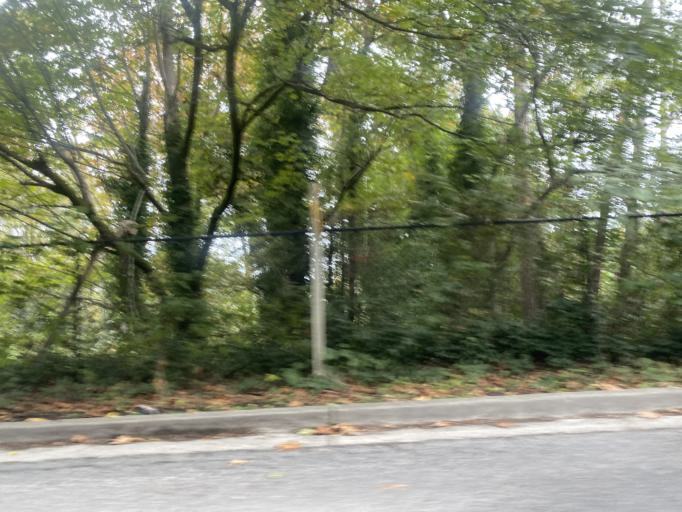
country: US
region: Washington
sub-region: King County
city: Seattle
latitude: 47.6643
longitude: -122.4082
